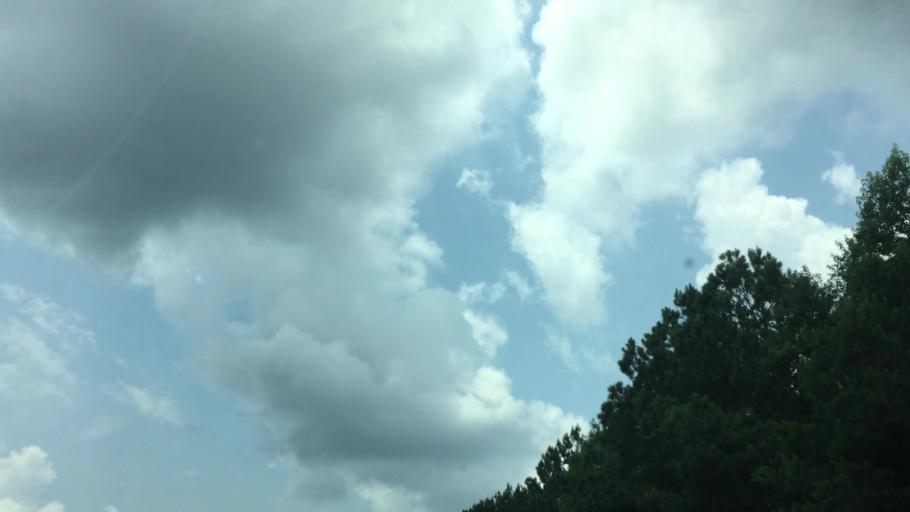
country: US
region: Georgia
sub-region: Fulton County
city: Palmetto
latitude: 33.5795
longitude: -84.6689
